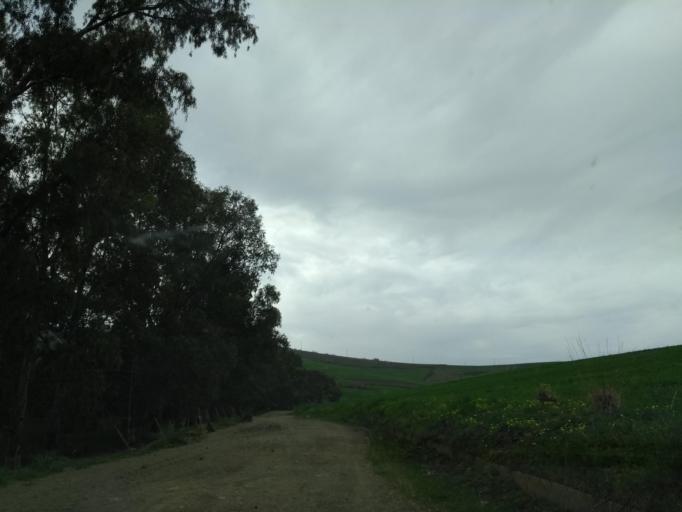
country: IT
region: Sicily
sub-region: Palermo
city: Partinico
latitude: 37.9888
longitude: 13.0817
